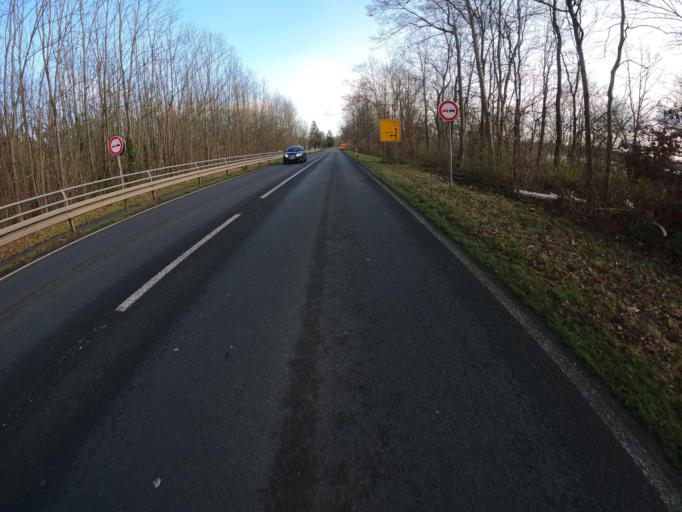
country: DE
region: Saxony
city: Markranstadt
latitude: 51.3177
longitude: 12.2470
